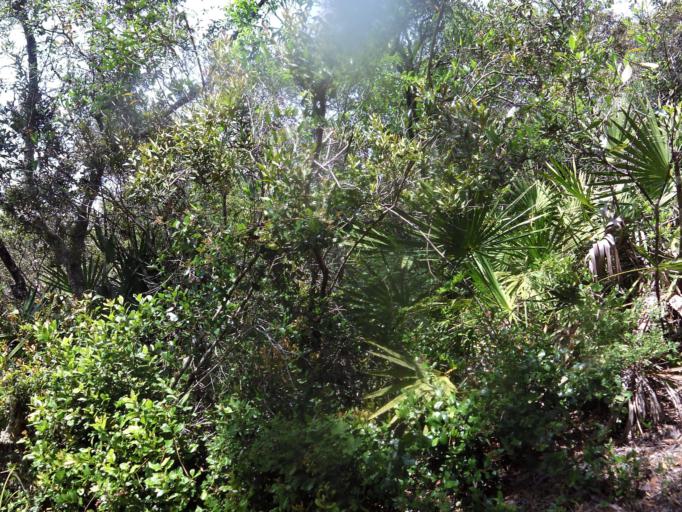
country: US
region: Florida
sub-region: Nassau County
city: Fernandina Beach
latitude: 30.4960
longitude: -81.4906
